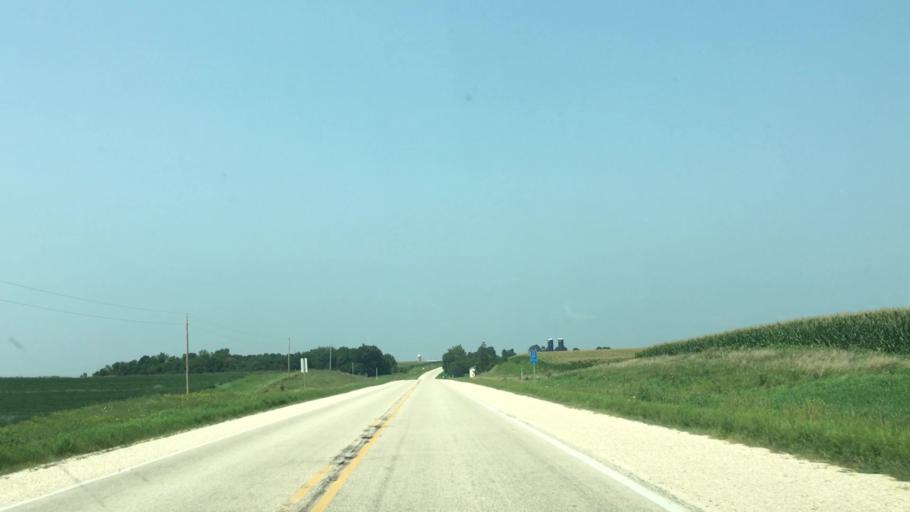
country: US
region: Iowa
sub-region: Fayette County
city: West Union
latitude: 42.9991
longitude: -91.8241
